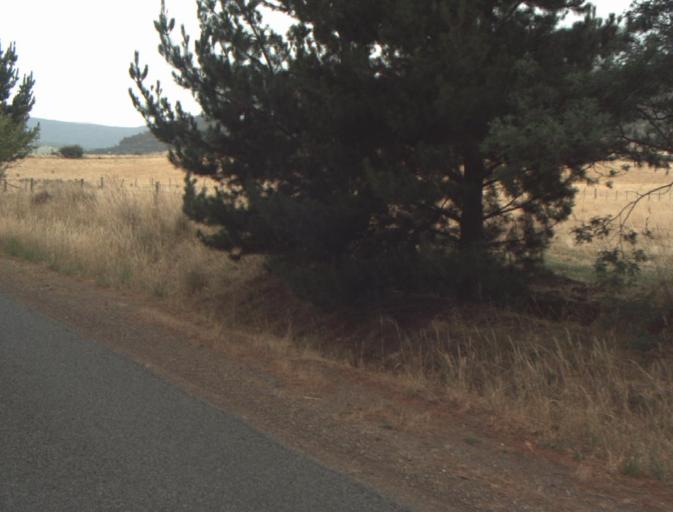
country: AU
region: Tasmania
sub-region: Northern Midlands
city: Evandale
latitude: -41.5040
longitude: 147.4789
